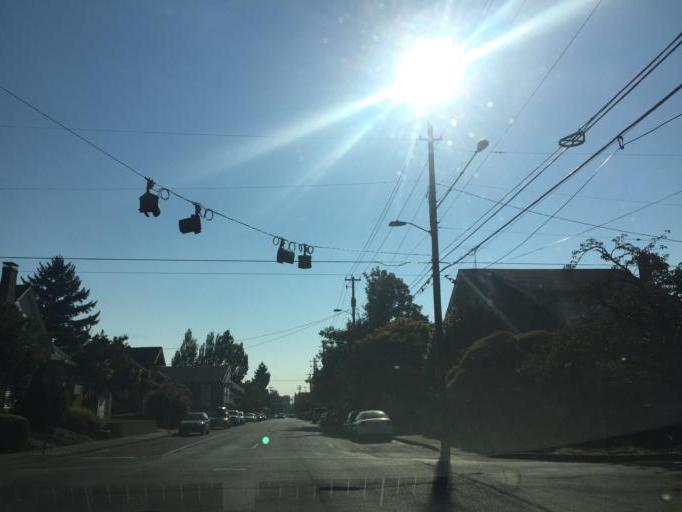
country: US
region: Oregon
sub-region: Multnomah County
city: Portland
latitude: 45.5378
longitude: -122.6252
